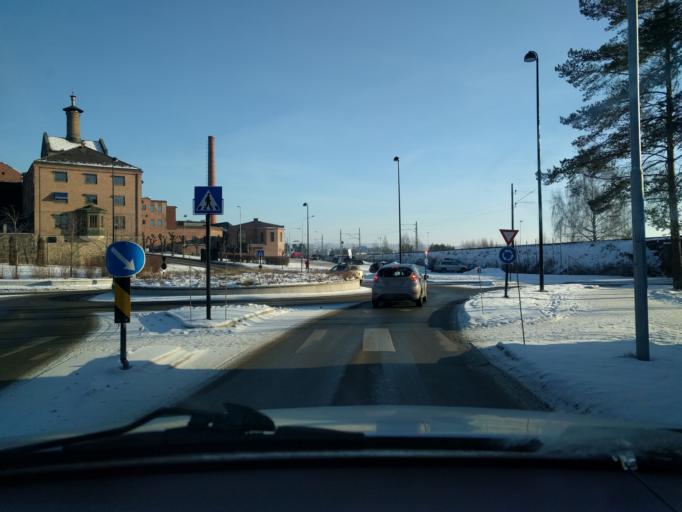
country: NO
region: Hedmark
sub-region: Hamar
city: Hamar
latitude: 60.7951
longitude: 11.0583
